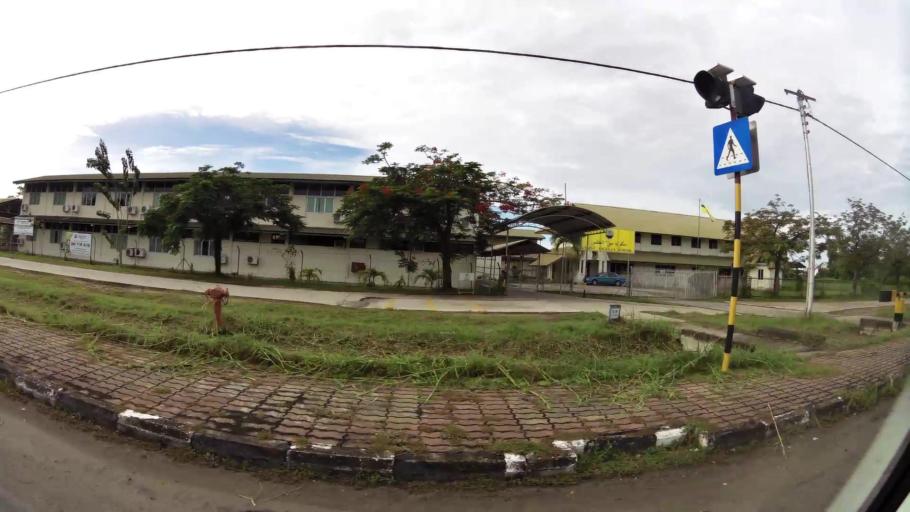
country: BN
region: Belait
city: Seria
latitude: 4.6143
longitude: 114.3377
